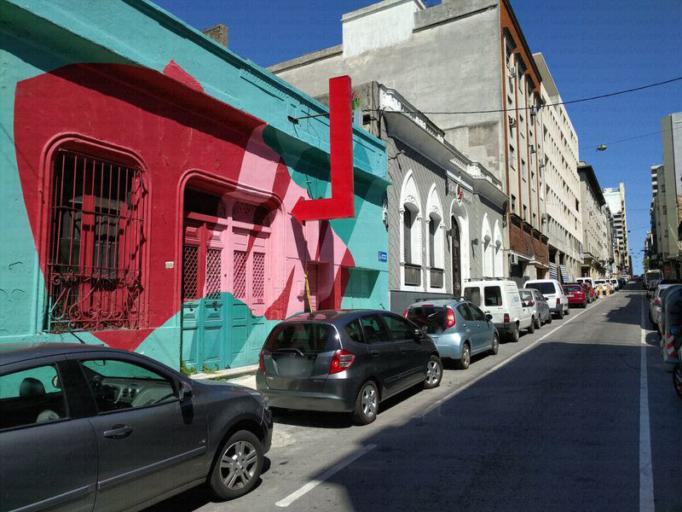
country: UY
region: Montevideo
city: Montevideo
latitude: -34.9036
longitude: -56.2045
